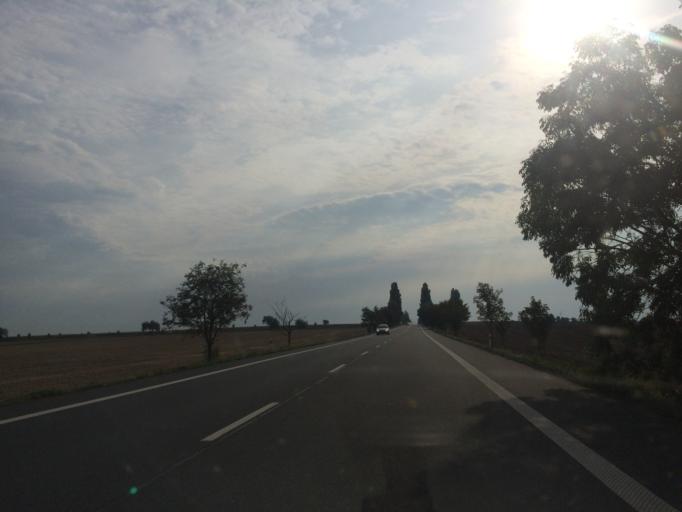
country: CZ
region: Central Bohemia
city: Poricany
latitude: 50.0515
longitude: 14.9294
